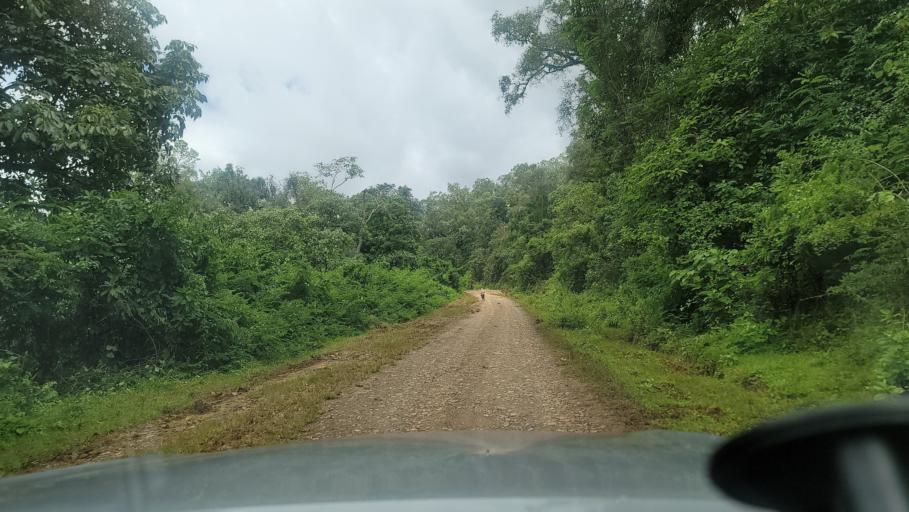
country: ET
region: Southern Nations, Nationalities, and People's Region
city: Bonga
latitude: 7.6297
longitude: 36.2182
